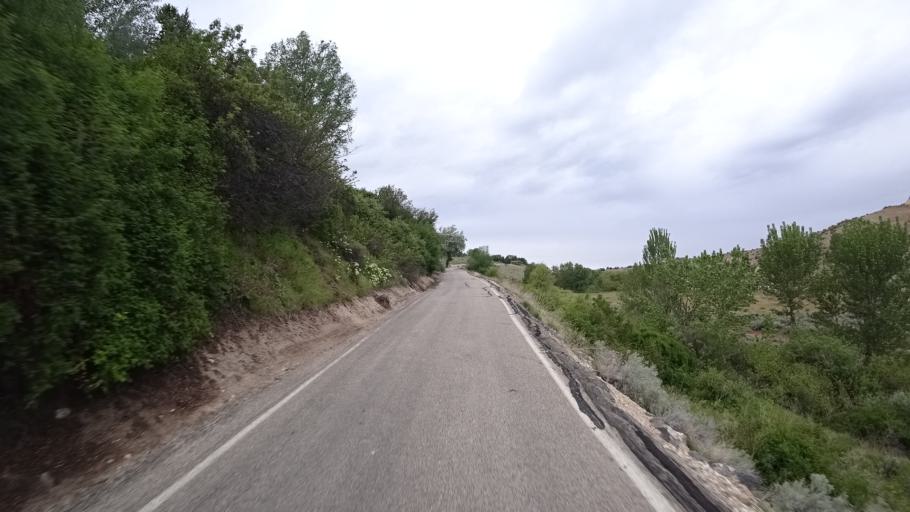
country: US
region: Idaho
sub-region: Ada County
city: Boise
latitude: 43.6161
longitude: -116.1611
